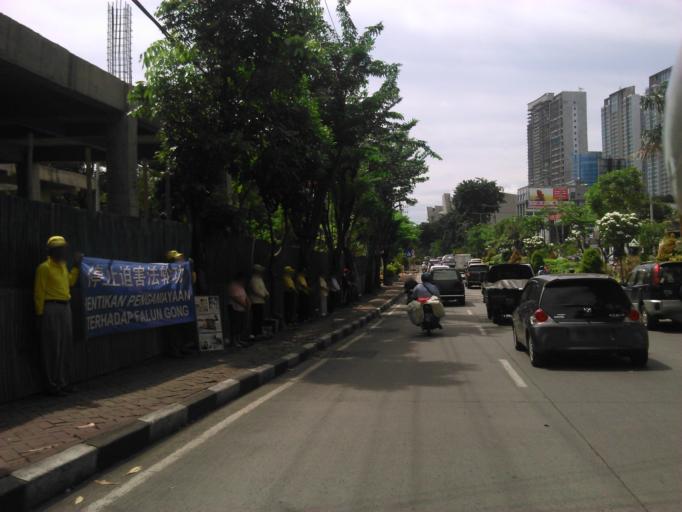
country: ID
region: East Java
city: Jagirsidosermo
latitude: -7.2908
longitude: 112.7149
